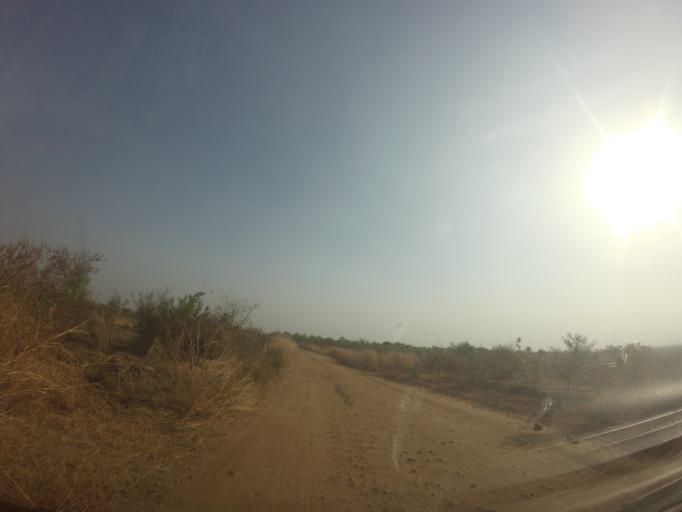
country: UG
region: Northern Region
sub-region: Maracha District
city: Maracha
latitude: 3.1165
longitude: 31.1567
